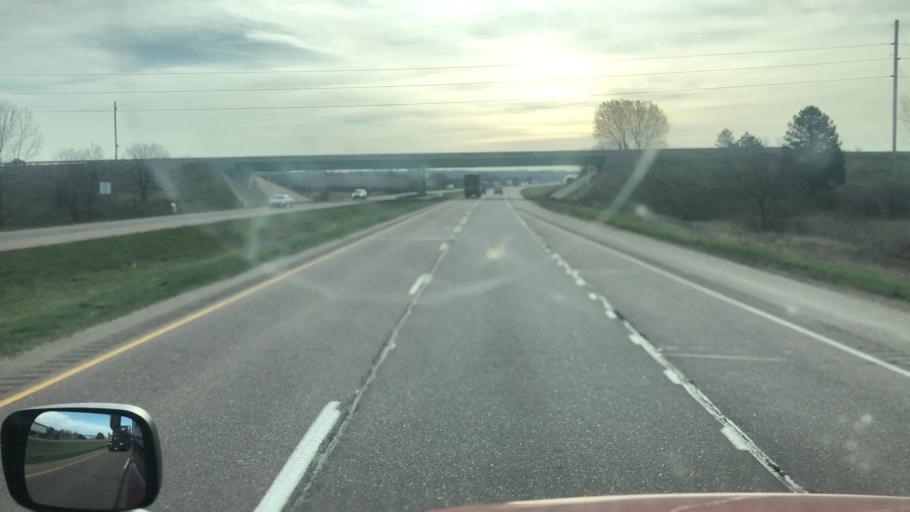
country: US
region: Nebraska
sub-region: Dakota County
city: South Sioux City
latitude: 42.4493
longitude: -96.4059
